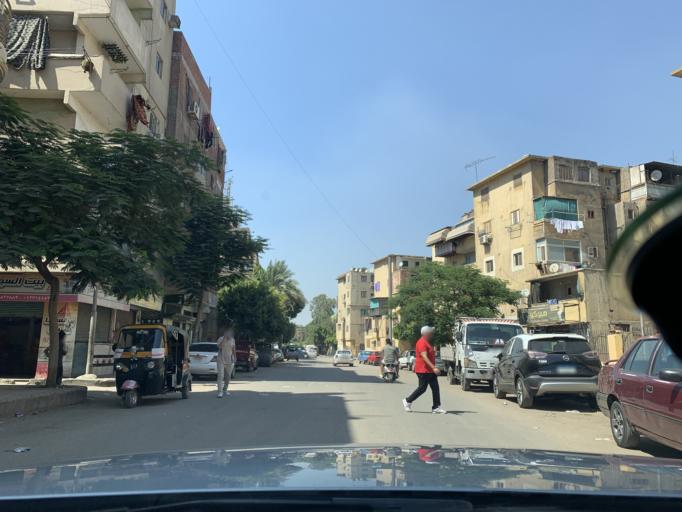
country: EG
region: Muhafazat al Qahirah
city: Cairo
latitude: 30.0729
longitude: 31.2569
